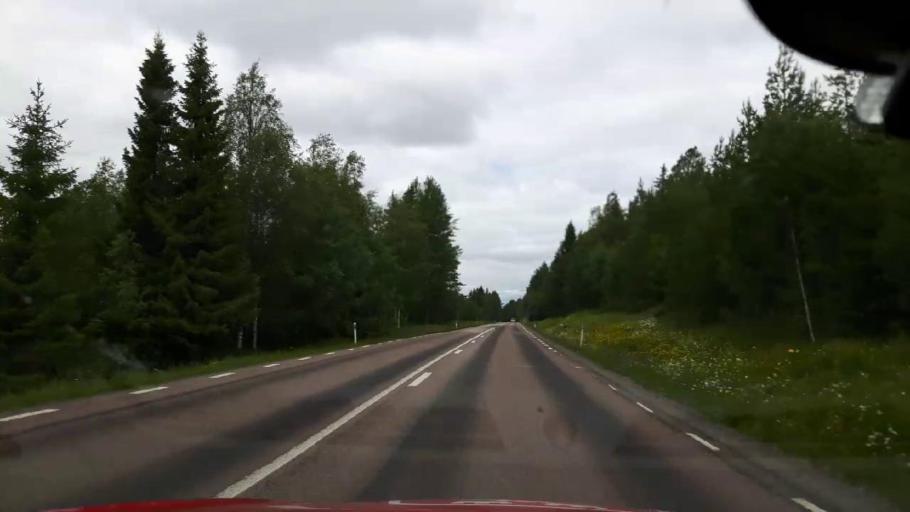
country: SE
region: Jaemtland
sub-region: OEstersunds Kommun
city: Brunflo
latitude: 62.9952
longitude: 14.9714
